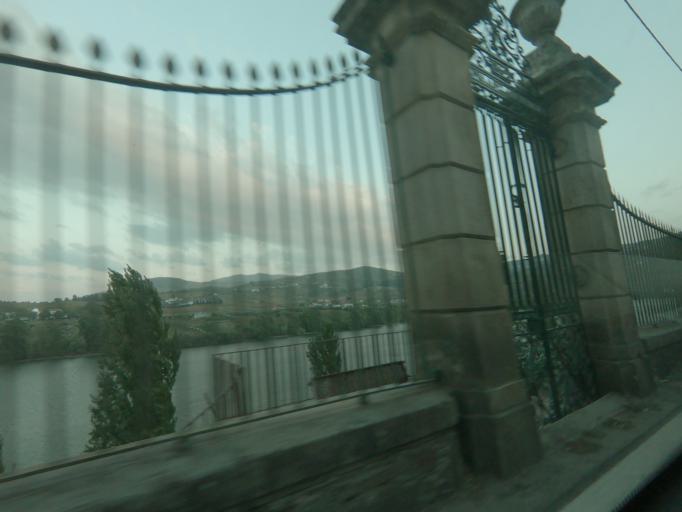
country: PT
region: Vila Real
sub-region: Peso da Regua
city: Godim
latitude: 41.1570
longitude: -7.8077
